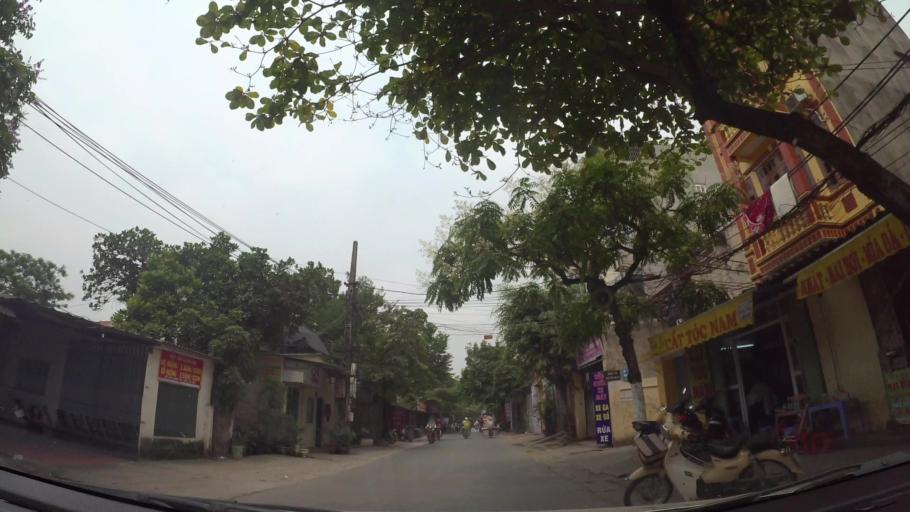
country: VN
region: Ha Noi
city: Ha Dong
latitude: 20.9709
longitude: 105.7667
